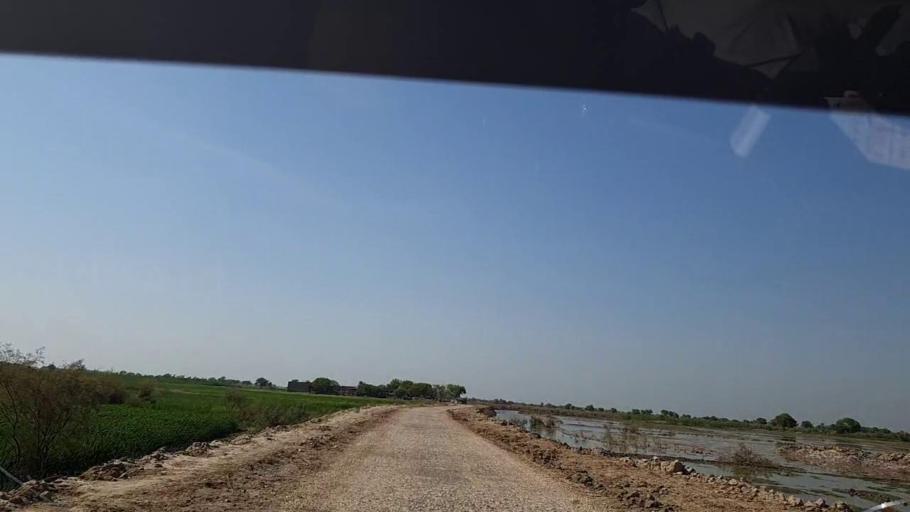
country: PK
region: Sindh
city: Tangwani
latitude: 28.3256
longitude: 69.0810
